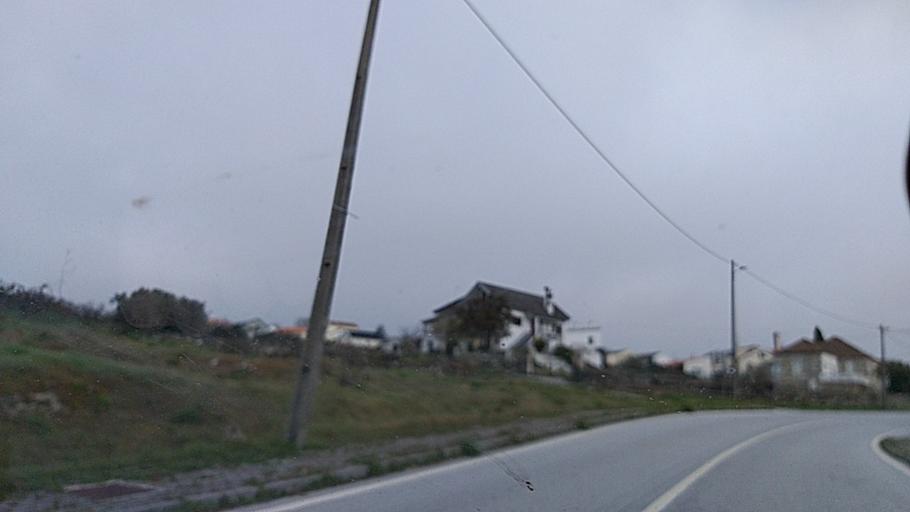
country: PT
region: Guarda
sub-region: Fornos de Algodres
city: Fornos de Algodres
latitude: 40.6812
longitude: -7.4708
